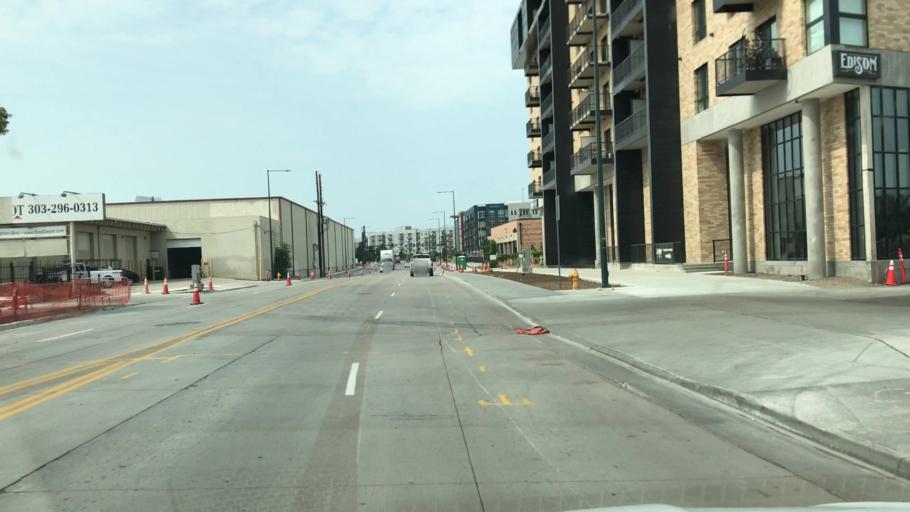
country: US
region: Colorado
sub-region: Denver County
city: Denver
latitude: 39.7663
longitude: -104.9842
